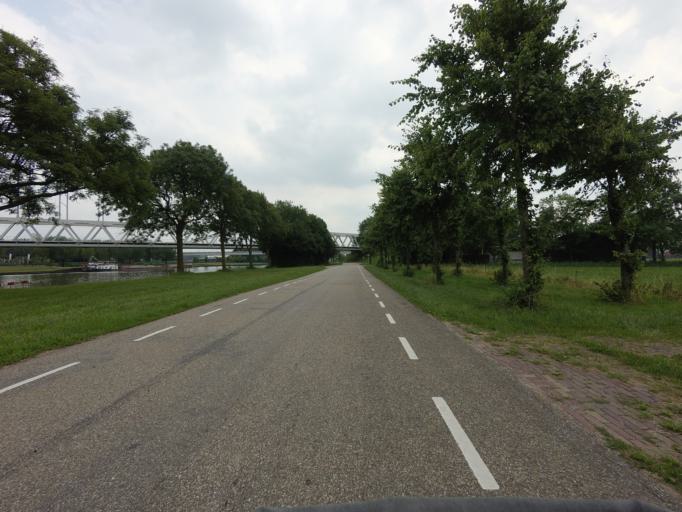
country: NL
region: Utrecht
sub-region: Gemeente Houten
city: Houten
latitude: 52.0055
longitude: 5.1834
